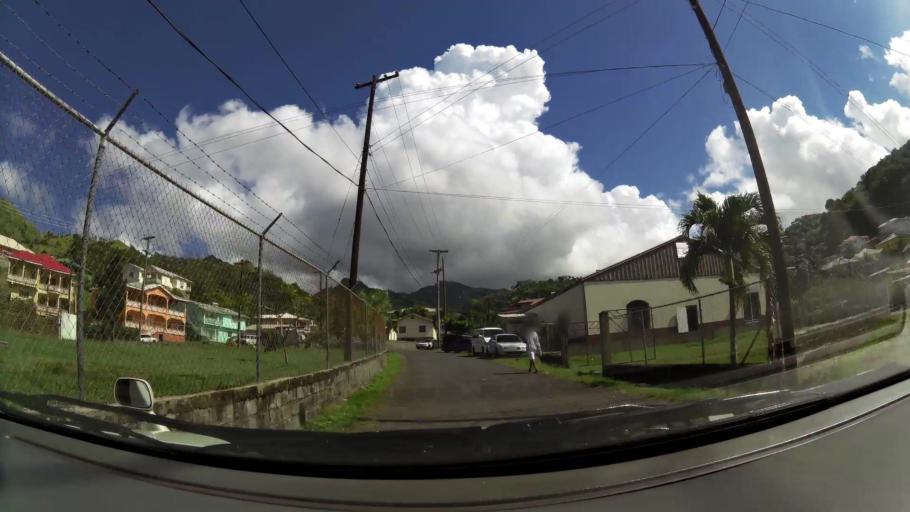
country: VC
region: Saint George
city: Kingstown Park
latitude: 13.1708
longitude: -61.2420
